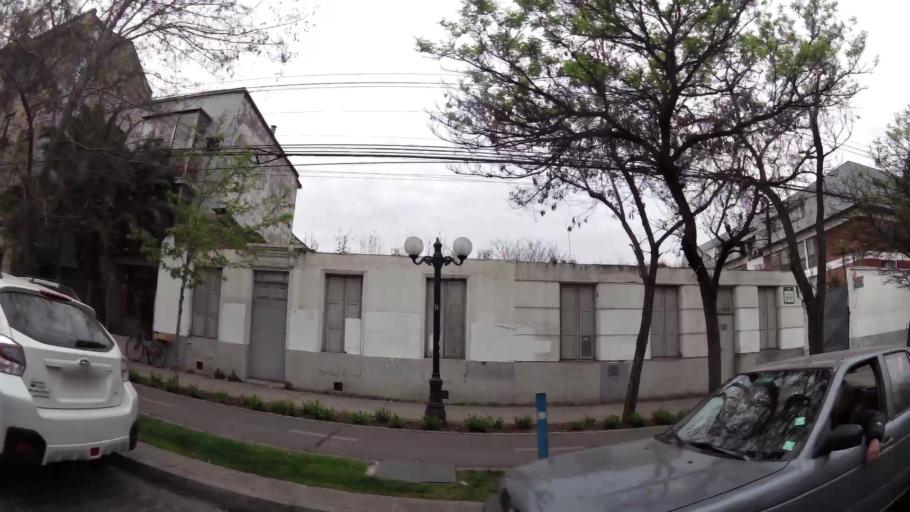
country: CL
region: Santiago Metropolitan
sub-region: Provincia de Santiago
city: Santiago
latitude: -33.4459
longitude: -70.6306
